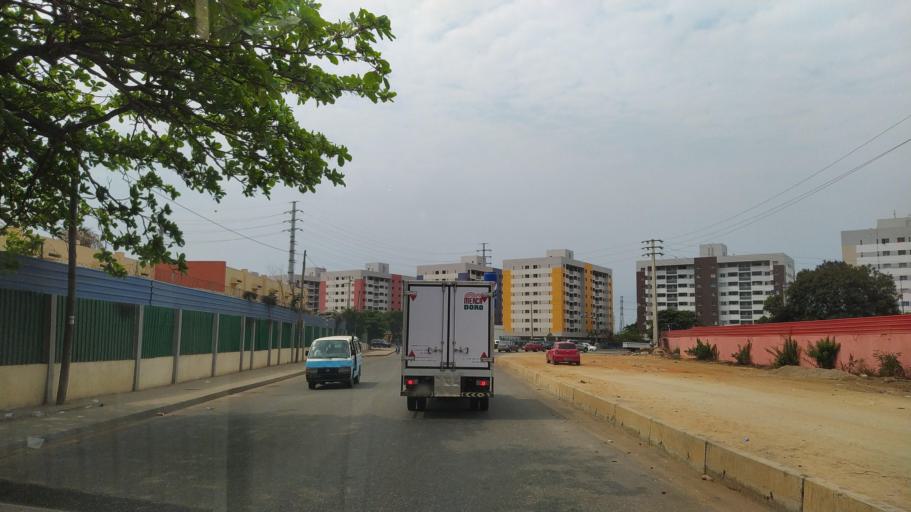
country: AO
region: Luanda
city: Luanda
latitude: -8.8533
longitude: 13.2888
